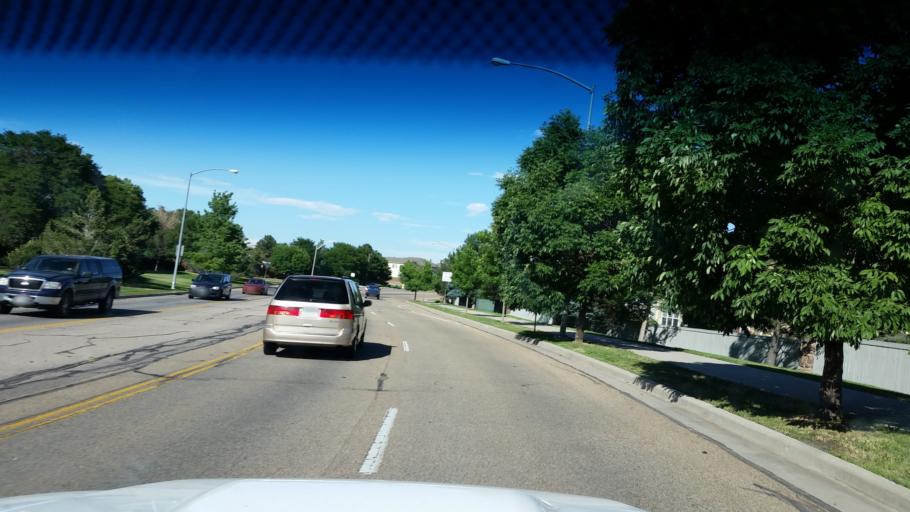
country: US
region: Colorado
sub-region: Adams County
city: Northglenn
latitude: 39.9272
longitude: -104.9455
